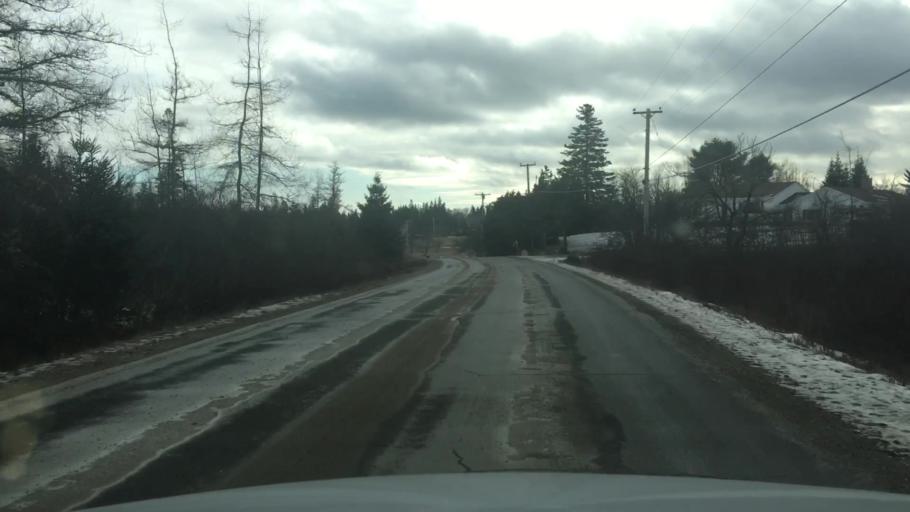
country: US
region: Maine
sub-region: Washington County
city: Machias
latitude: 44.6189
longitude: -67.4798
